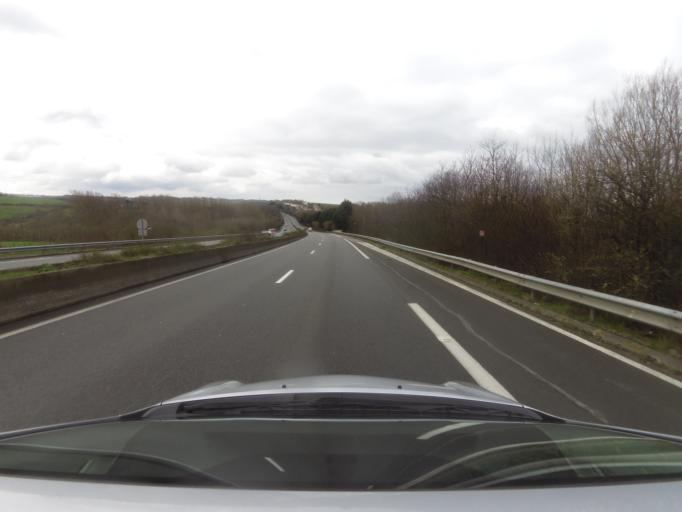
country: FR
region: Nord-Pas-de-Calais
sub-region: Departement du Pas-de-Calais
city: Wimille
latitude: 50.7657
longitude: 1.6393
